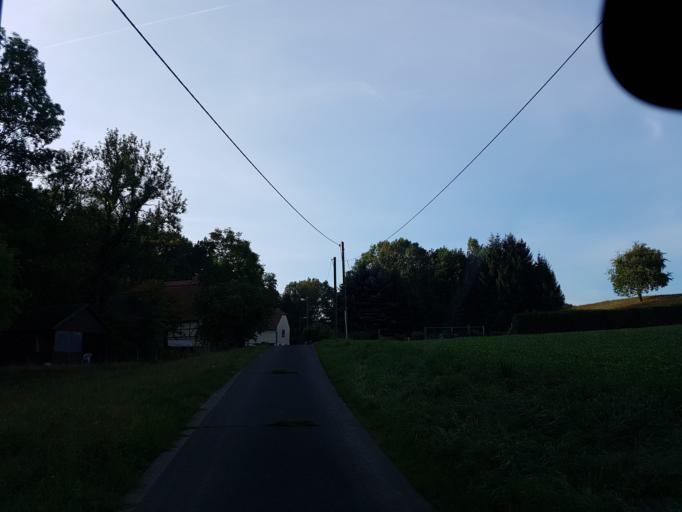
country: DE
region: Saxony
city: Dobeln
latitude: 51.1173
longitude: 13.0678
